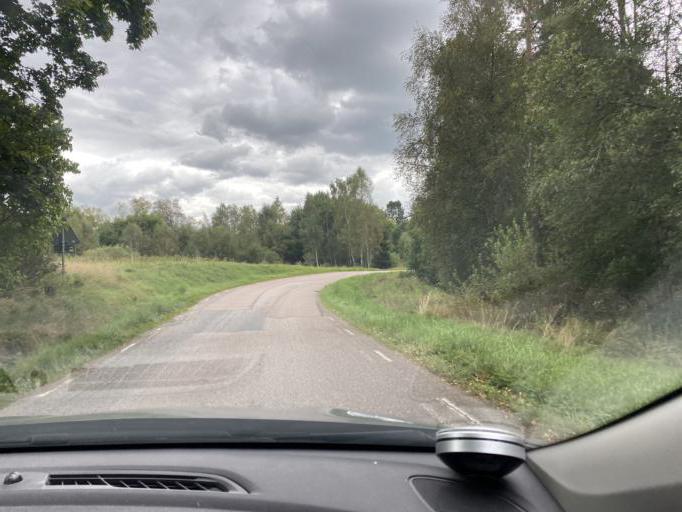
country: SE
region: Kronoberg
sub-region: Markaryds Kommun
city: Markaryd
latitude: 56.4729
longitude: 13.5666
